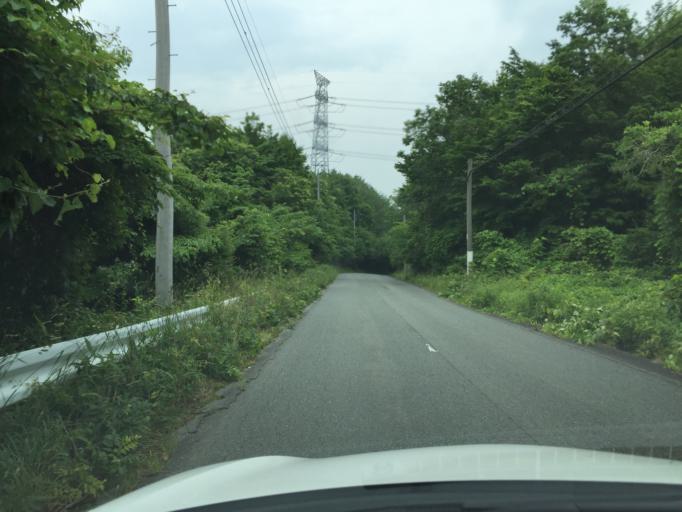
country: JP
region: Fukushima
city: Iwaki
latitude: 37.1581
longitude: 140.7011
